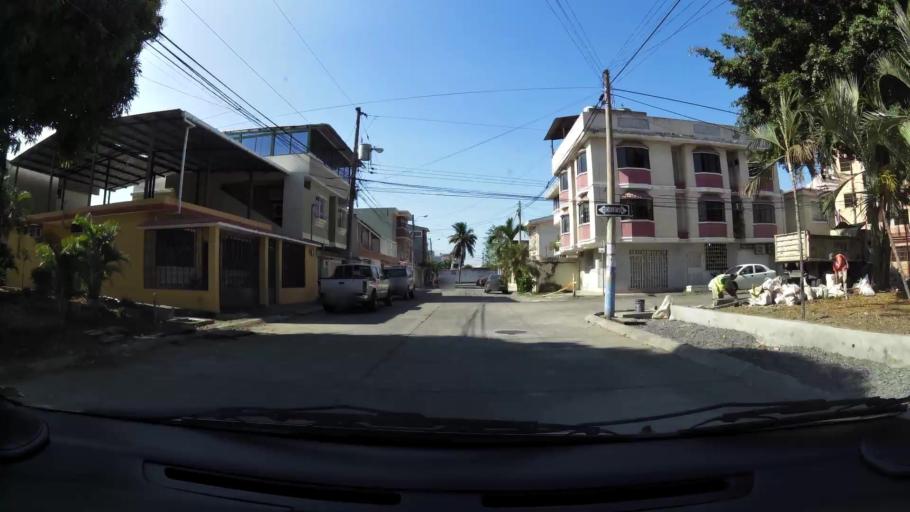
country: EC
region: Guayas
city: Eloy Alfaro
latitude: -2.1472
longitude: -79.9035
